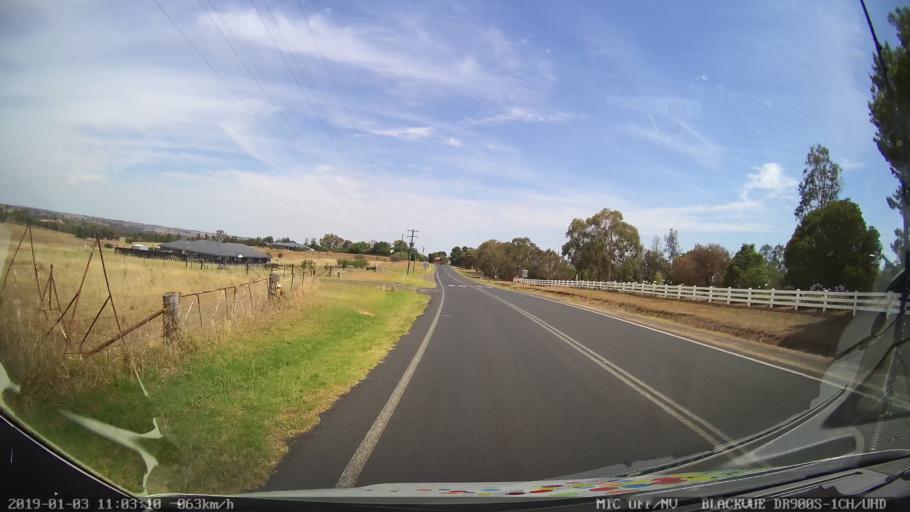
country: AU
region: New South Wales
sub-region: Young
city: Young
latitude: -34.2927
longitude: 148.2962
